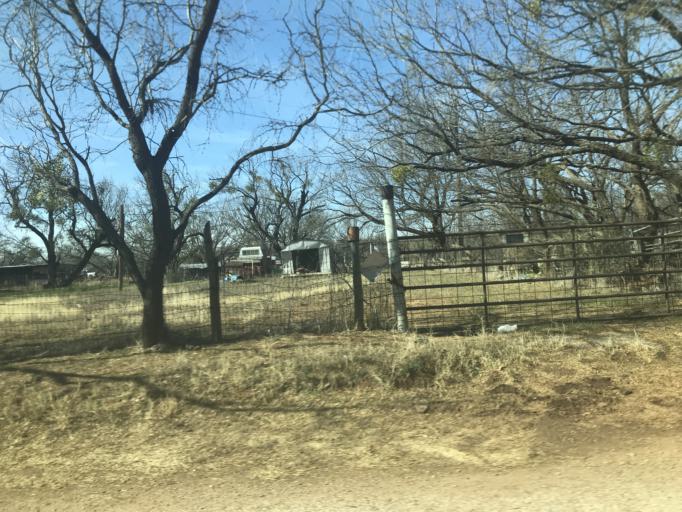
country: US
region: Texas
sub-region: Taylor County
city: Abilene
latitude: 32.4963
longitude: -99.7426
